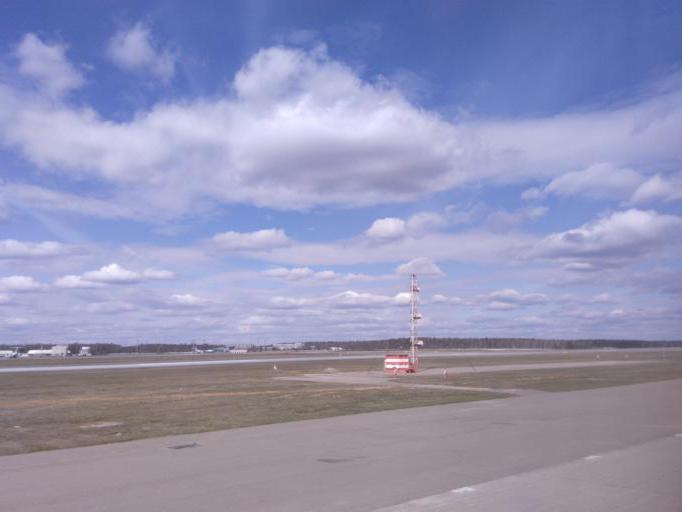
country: RU
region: Moskovskaya
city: Sheremet'yevskiy
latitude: 55.9727
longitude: 37.4380
